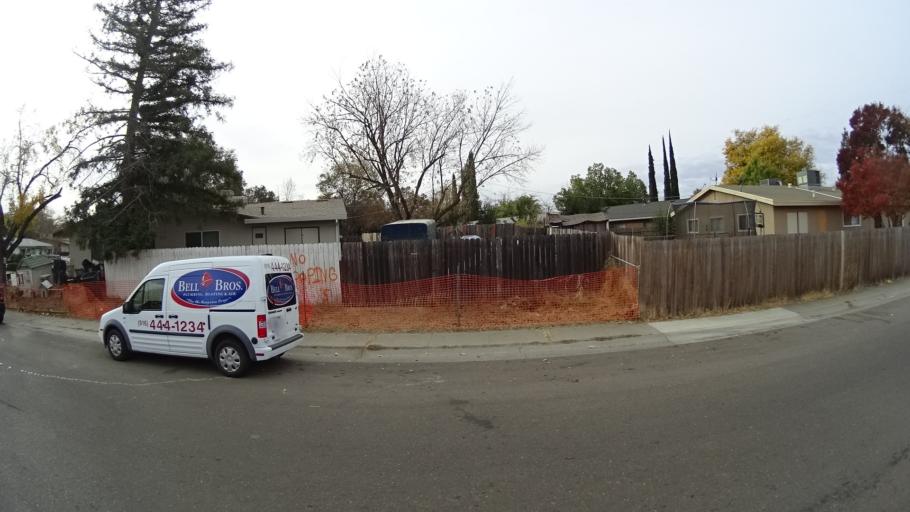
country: US
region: California
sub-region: Sacramento County
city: Citrus Heights
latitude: 38.7161
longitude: -121.2932
